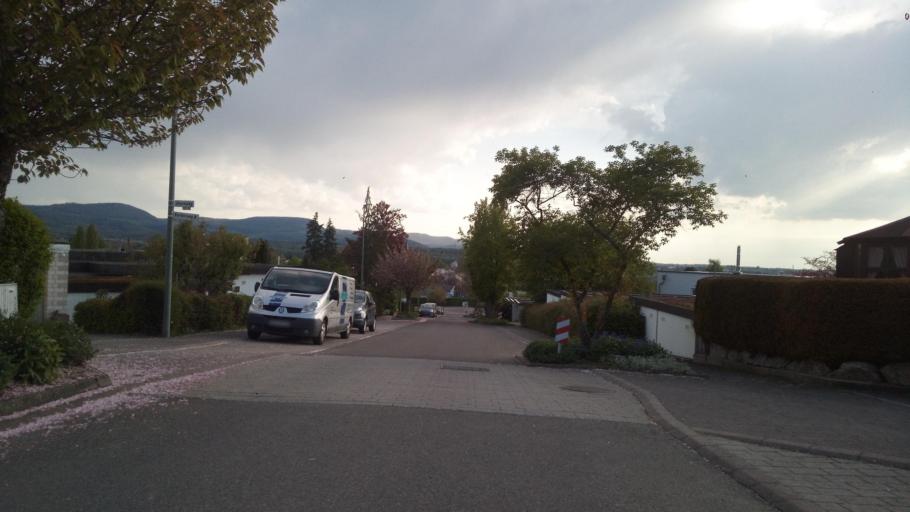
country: DE
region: Baden-Wuerttemberg
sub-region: Regierungsbezirk Stuttgart
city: Salach
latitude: 48.6966
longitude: 9.7482
